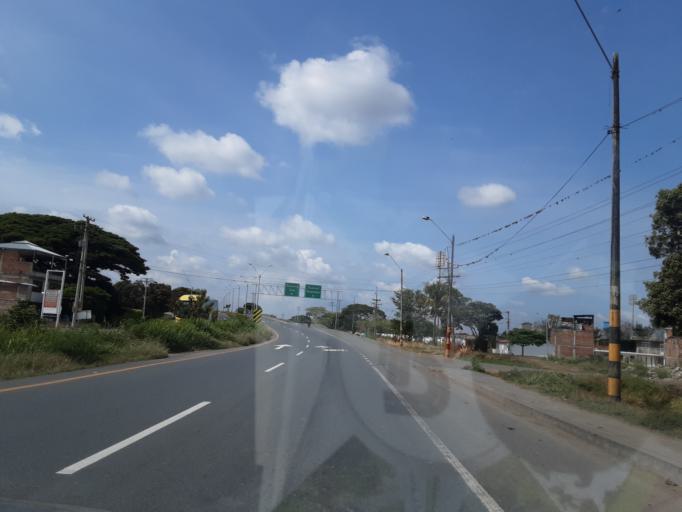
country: CO
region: Valle del Cauca
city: Guacari
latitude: 3.7657
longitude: -76.3271
